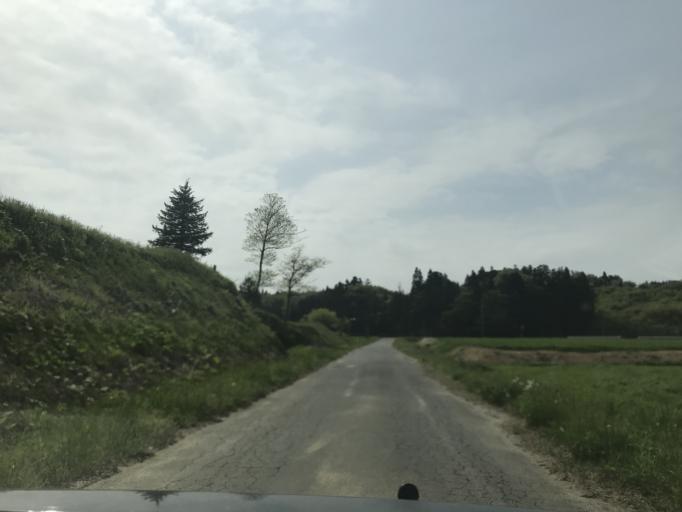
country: JP
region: Iwate
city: Ichinoseki
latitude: 38.8808
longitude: 141.0610
